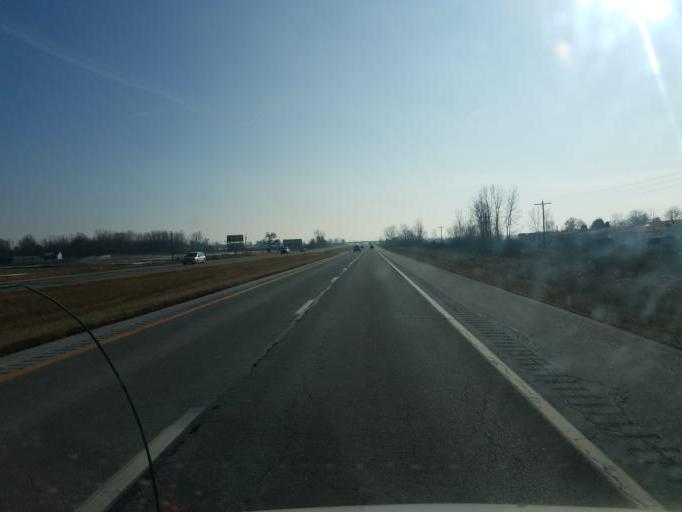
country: US
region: Ohio
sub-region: Marion County
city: Marion
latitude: 40.6266
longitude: -83.0966
